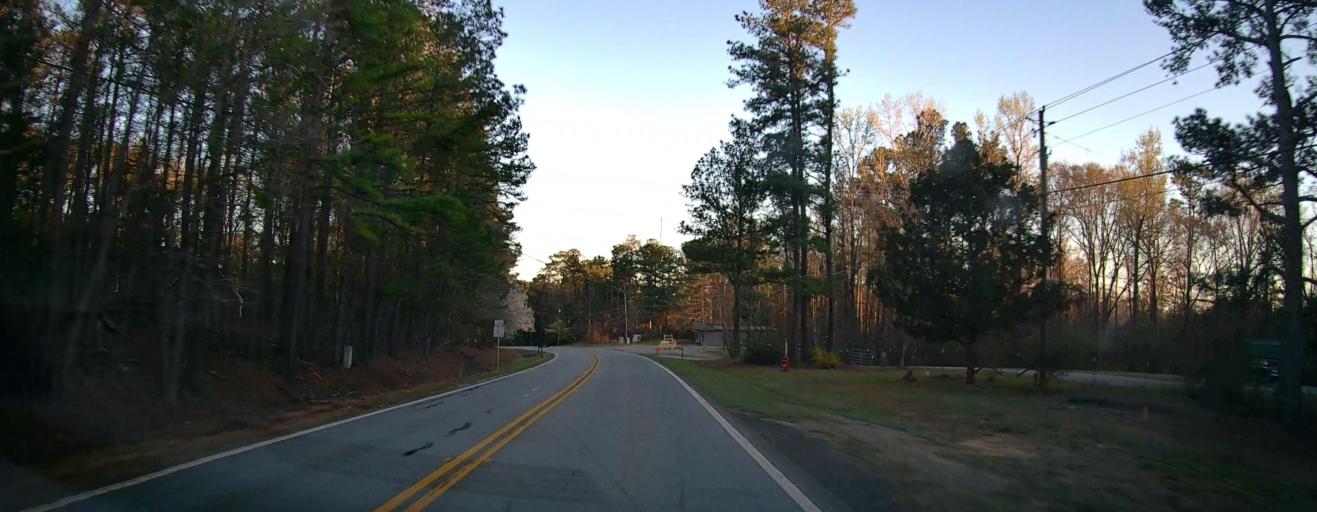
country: US
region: Alabama
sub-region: Lee County
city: Smiths Station
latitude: 32.6244
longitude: -85.0355
